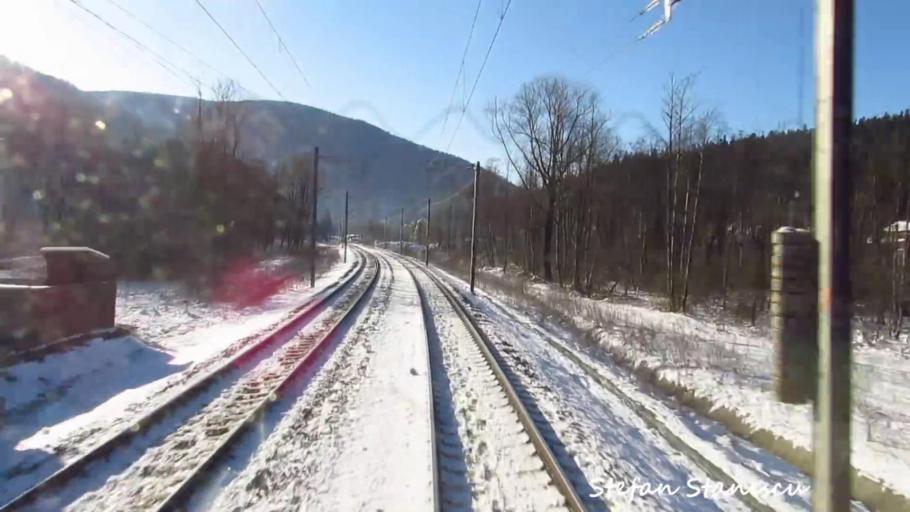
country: RO
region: Prahova
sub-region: Oras Busteni
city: Poiana Tapului
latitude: 45.3719
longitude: 25.5436
